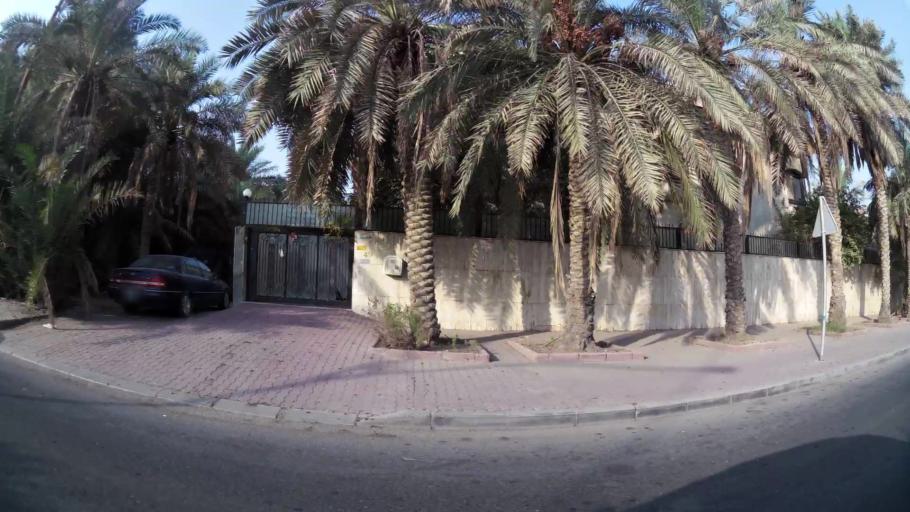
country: KW
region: Muhafazat Hawalli
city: Salwa
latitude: 29.2969
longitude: 48.0745
